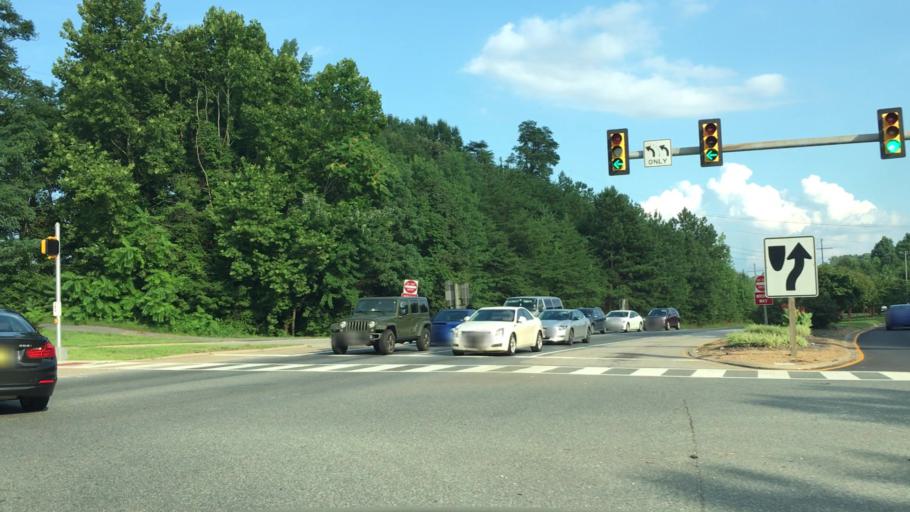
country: US
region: Virginia
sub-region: City of Fredericksburg
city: Fredericksburg
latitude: 38.2947
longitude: -77.4809
